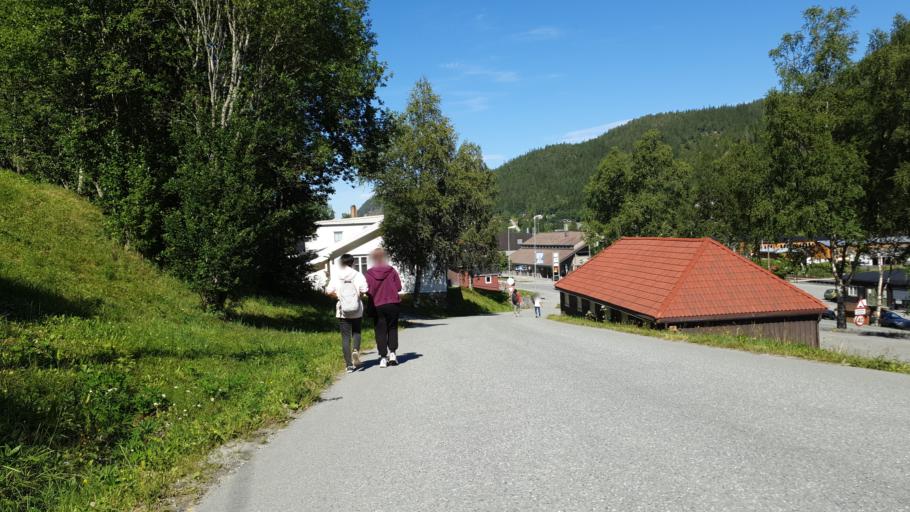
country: NO
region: Sor-Trondelag
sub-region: Meldal
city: Meldal
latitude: 63.1251
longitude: 9.7035
